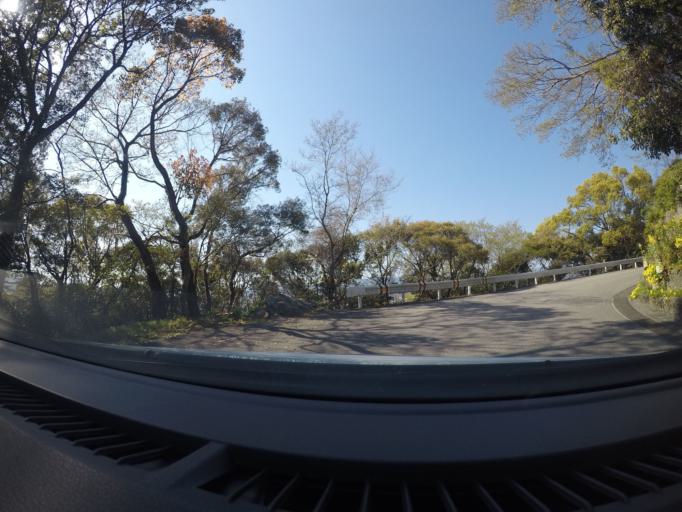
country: JP
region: Kochi
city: Kochi-shi
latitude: 33.5491
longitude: 133.5687
